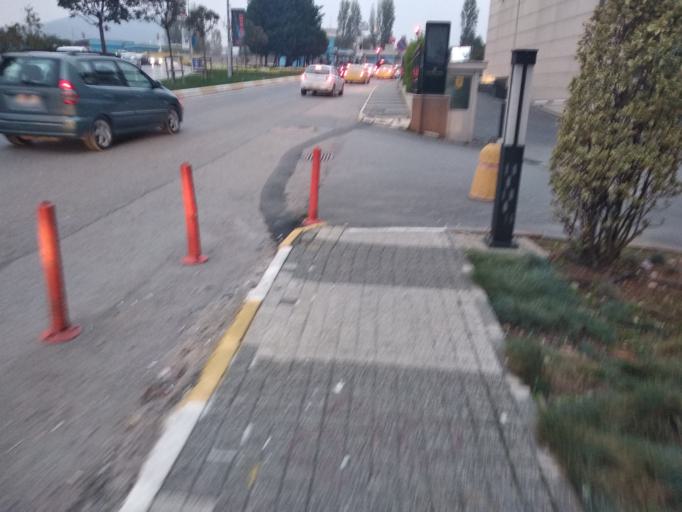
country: TR
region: Istanbul
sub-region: Atasehir
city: Atasehir
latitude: 40.9833
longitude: 29.1334
